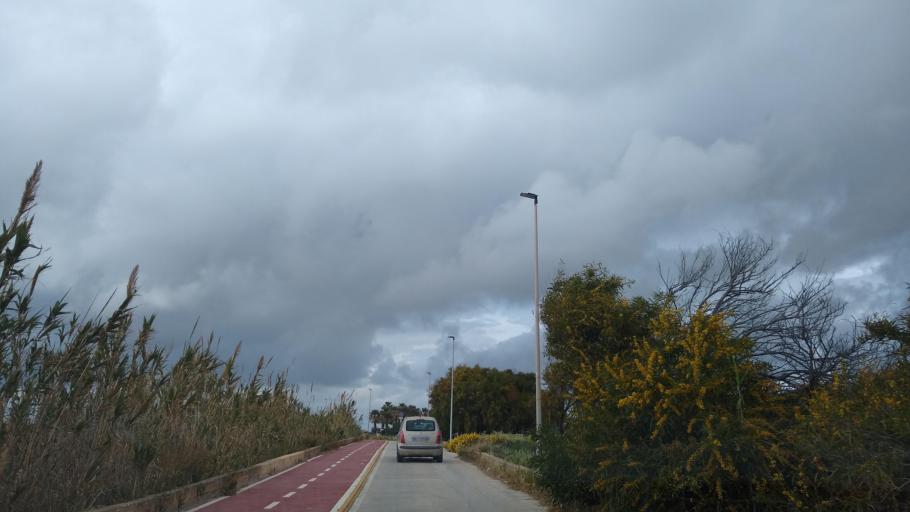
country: IT
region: Sicily
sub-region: Trapani
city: Marsala
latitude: 37.8602
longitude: 12.4852
